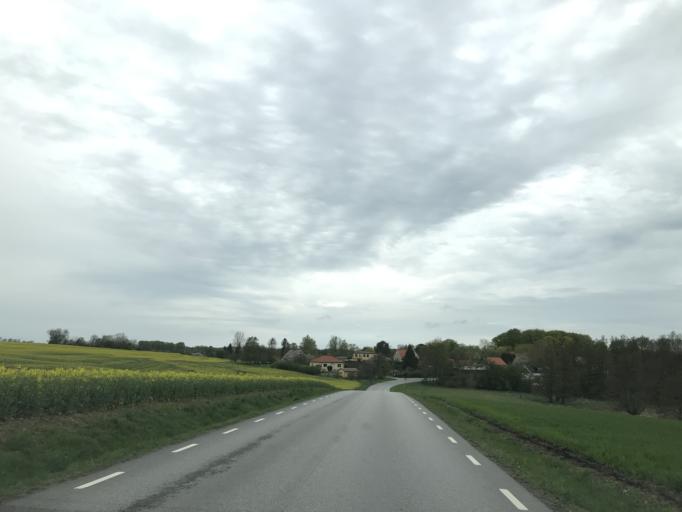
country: SE
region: Skane
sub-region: Trelleborgs Kommun
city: Anderslov
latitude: 55.4945
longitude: 13.3339
